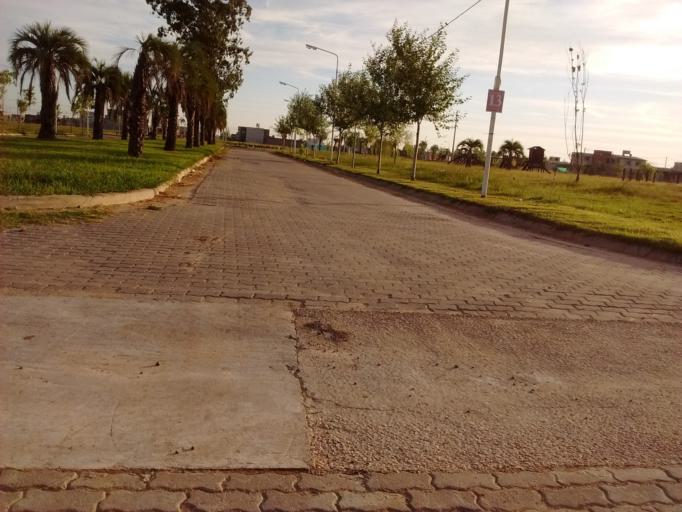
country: AR
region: Santa Fe
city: Roldan
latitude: -32.9344
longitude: -60.8764
